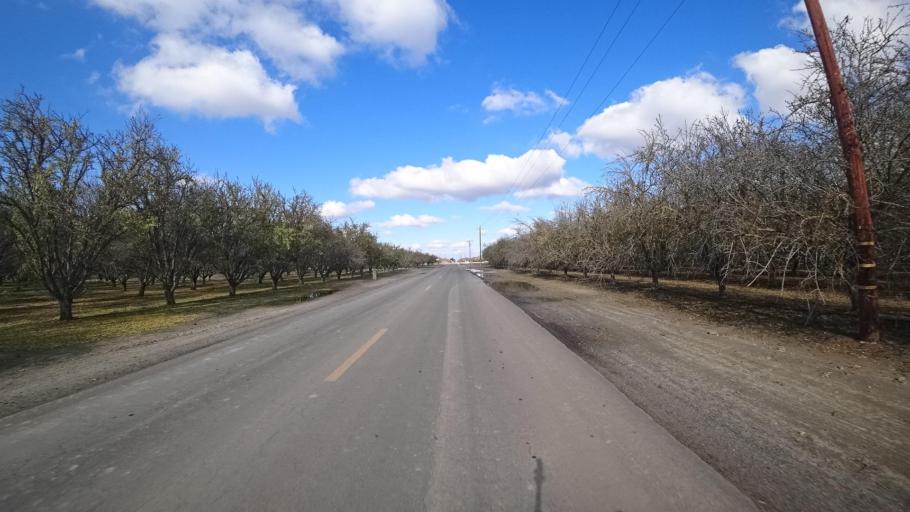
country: US
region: California
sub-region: Kern County
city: Delano
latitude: 35.7204
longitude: -119.3659
